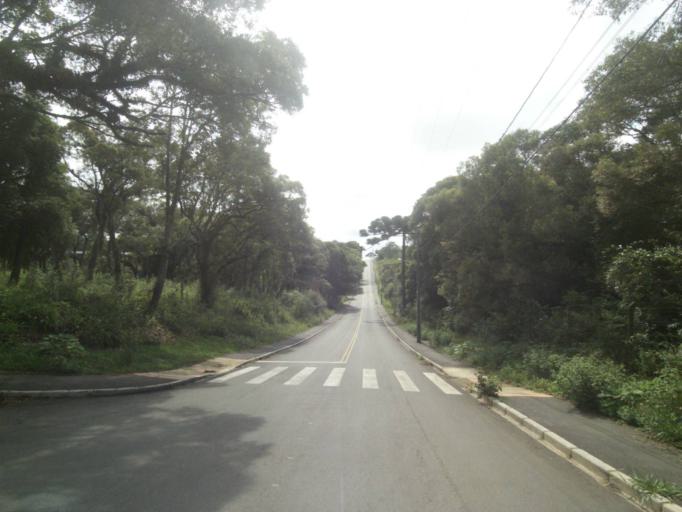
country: BR
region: Parana
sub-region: Quatro Barras
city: Quatro Barras
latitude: -25.3446
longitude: -49.0876
